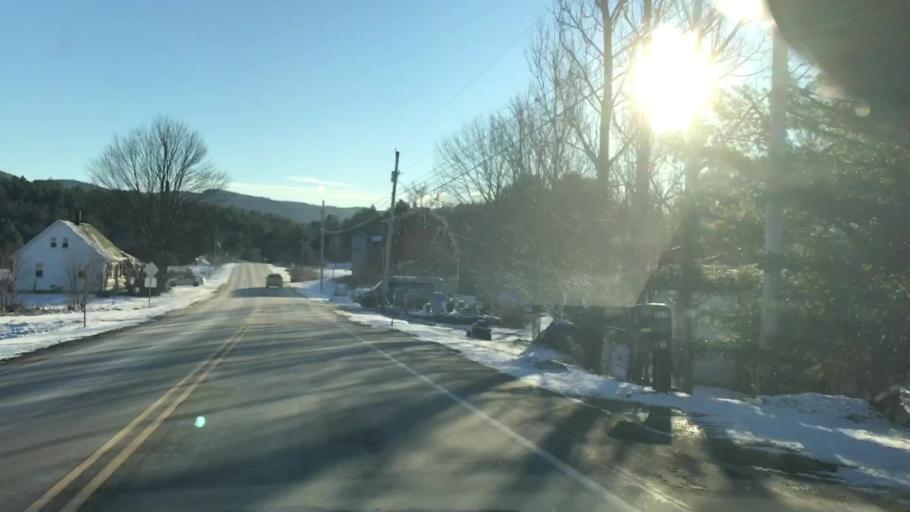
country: US
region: New Hampshire
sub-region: Grafton County
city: Haverhill
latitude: 43.9667
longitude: -72.0816
